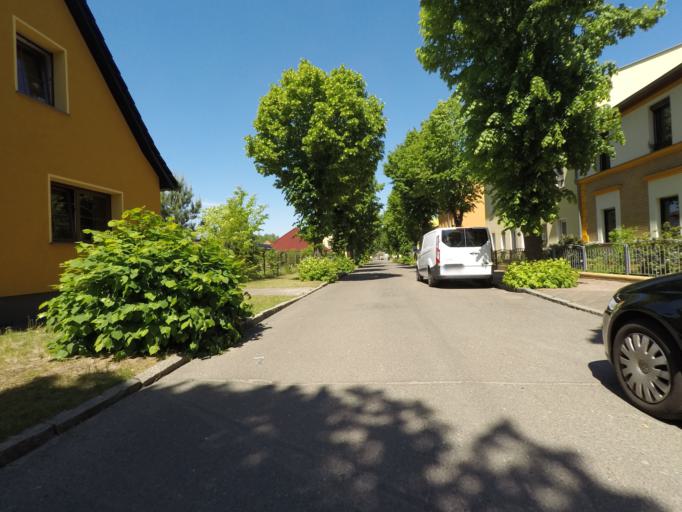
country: DE
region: Brandenburg
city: Melchow
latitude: 52.8380
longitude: 13.7268
